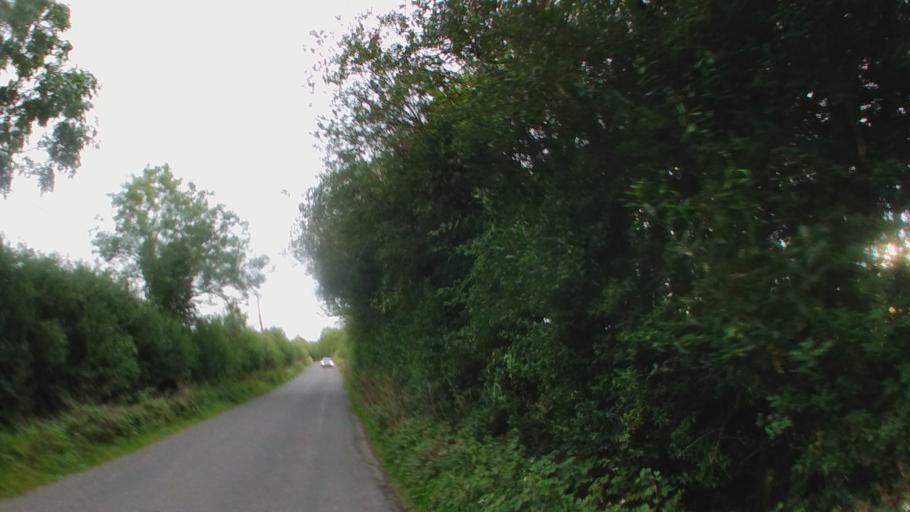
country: IE
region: Leinster
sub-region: Kilkenny
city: Kilkenny
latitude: 52.6826
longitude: -7.2207
